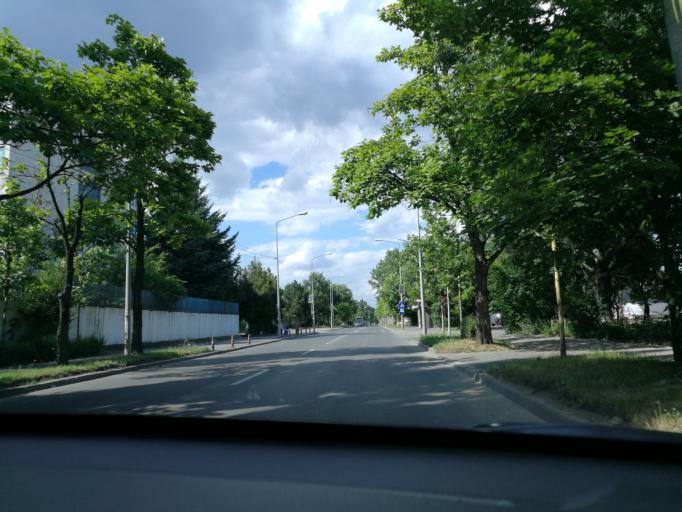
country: RO
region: Ilfov
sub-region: Comuna Glina
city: Catelu
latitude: 44.4199
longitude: 26.2186
